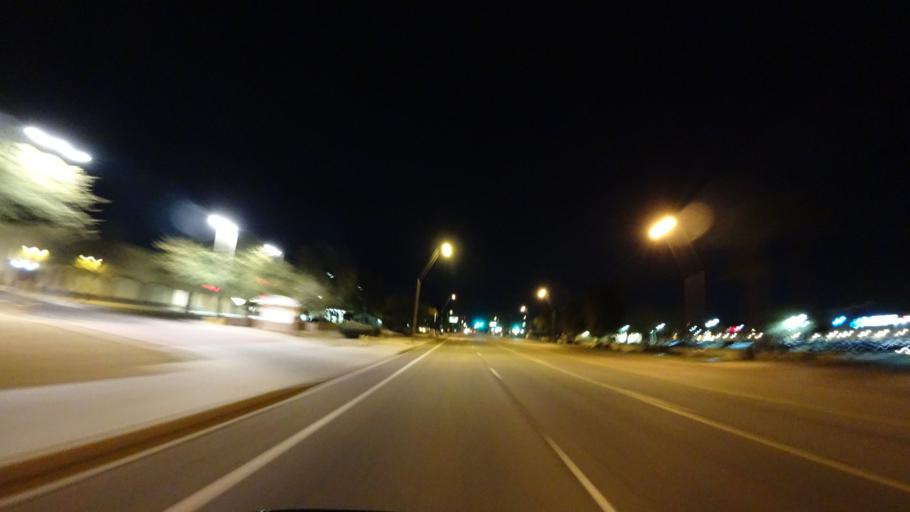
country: US
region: Arizona
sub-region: Maricopa County
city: San Carlos
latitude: 33.3346
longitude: -111.9094
